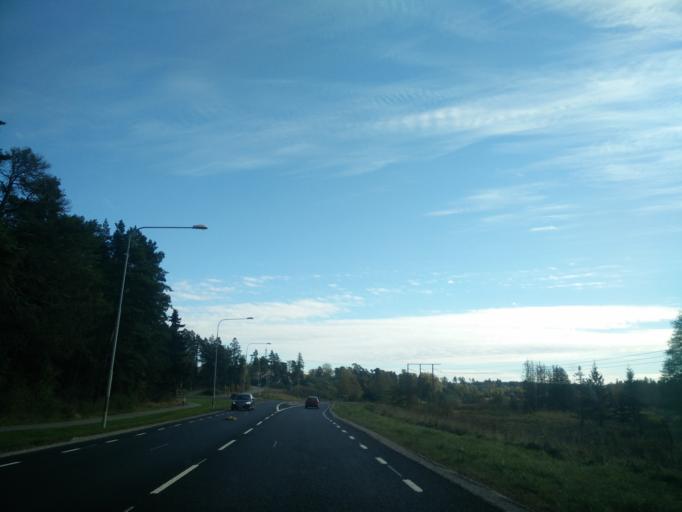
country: SE
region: Stockholm
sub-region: Upplands Vasby Kommun
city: Upplands Vaesby
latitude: 59.5103
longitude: 17.9597
